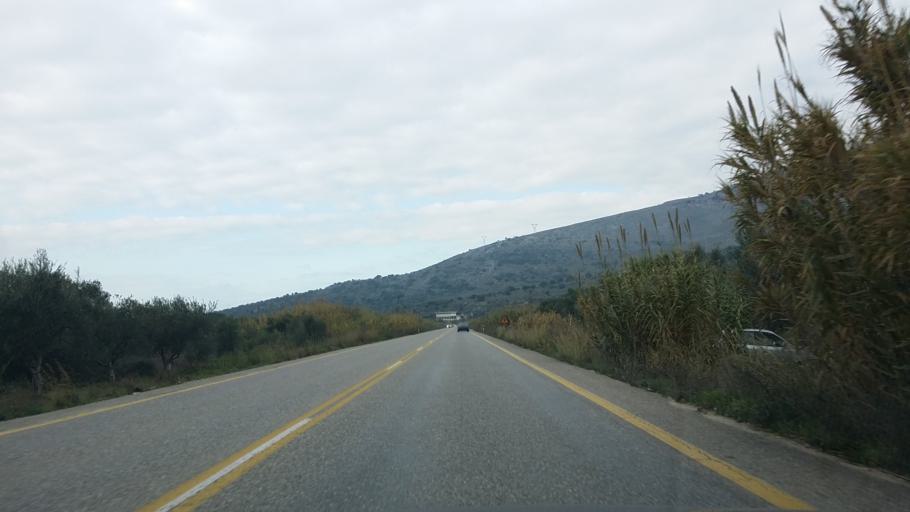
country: GR
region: West Greece
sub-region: Nomos Aitolias kai Akarnanias
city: Mesolongi
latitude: 38.4045
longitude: 21.4032
